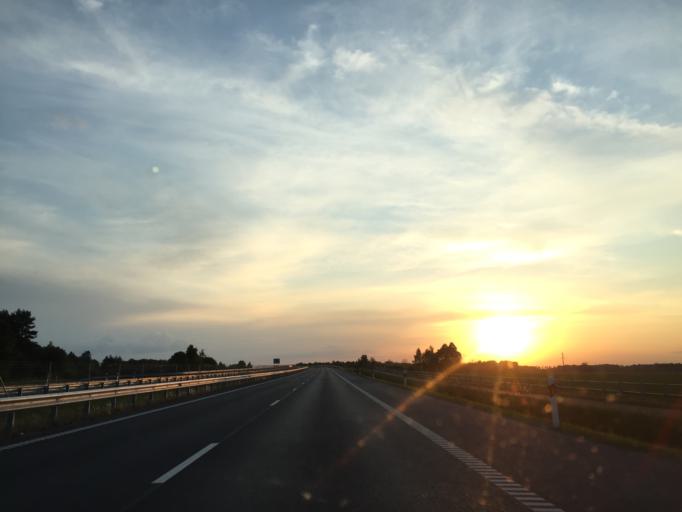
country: LT
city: Kursenai
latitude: 55.9869
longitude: 23.0827
